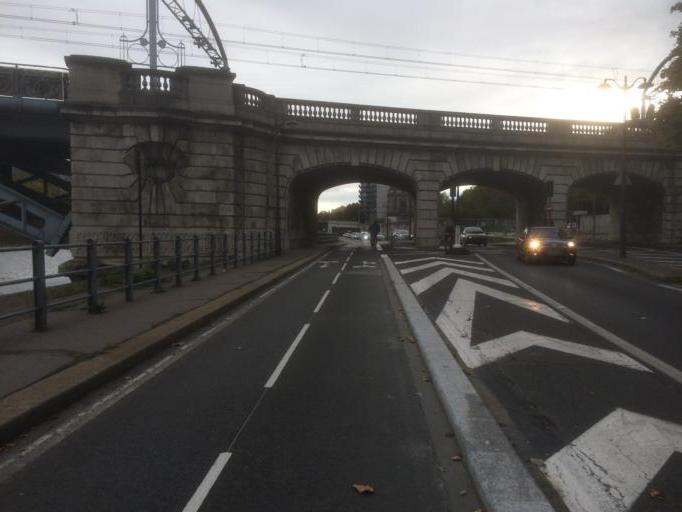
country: FR
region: Ile-de-France
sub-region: Departement des Hauts-de-Seine
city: Vanves
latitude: 48.8530
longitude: 2.2819
